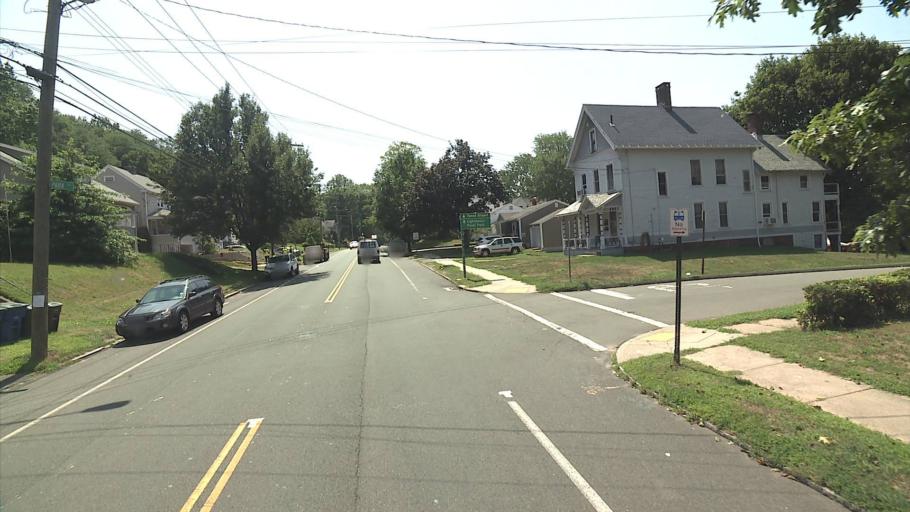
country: US
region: Connecticut
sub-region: New Haven County
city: East Haven
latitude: 41.2849
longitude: -72.8935
